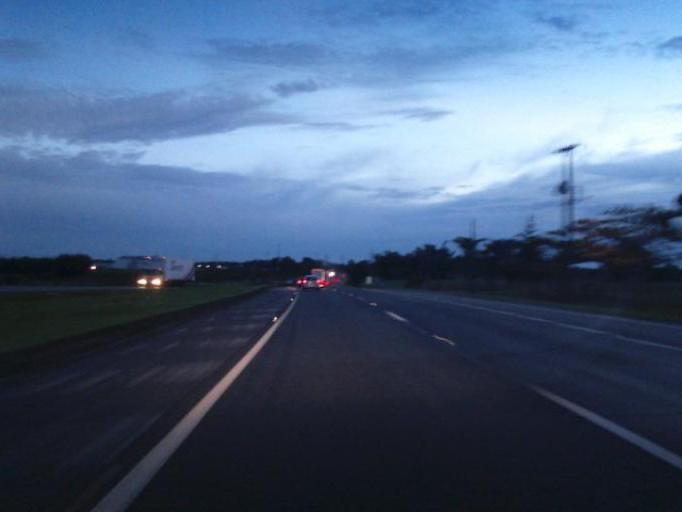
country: BR
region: Santa Catarina
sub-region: Barra Velha
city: Barra Velha
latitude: -26.4872
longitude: -48.7346
